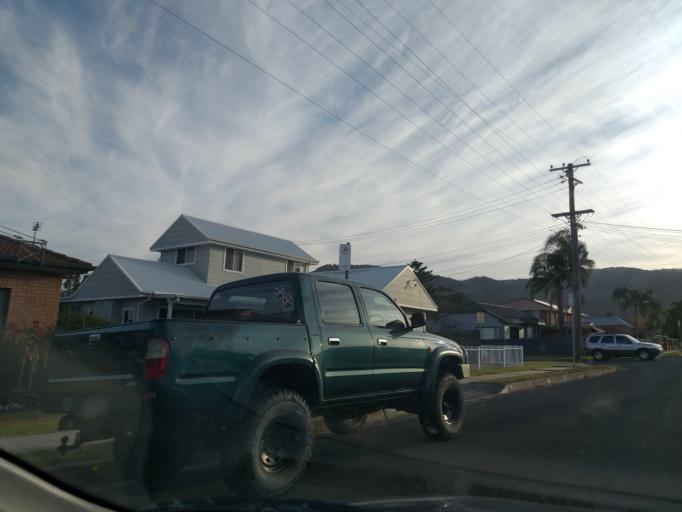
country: AU
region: New South Wales
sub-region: Wollongong
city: Fairy Meadow
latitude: -34.3883
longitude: 150.8869
